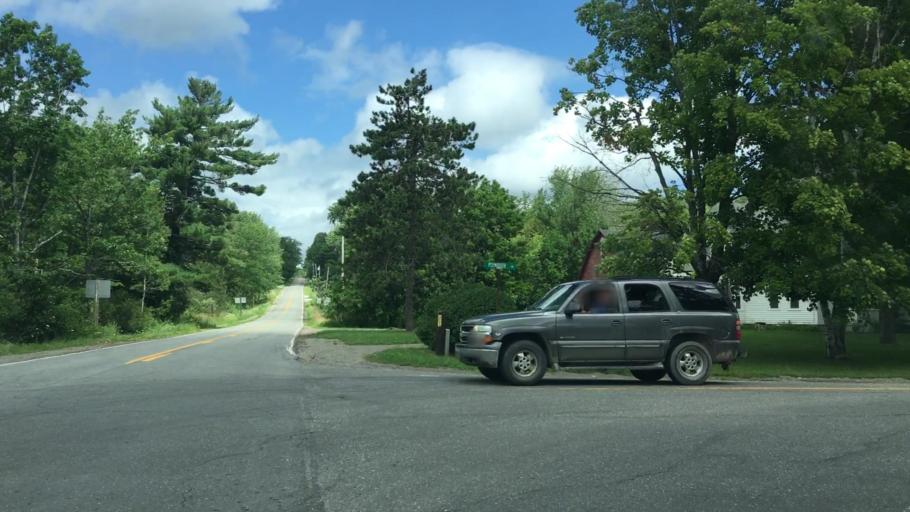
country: US
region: Maine
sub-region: Penobscot County
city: Etna
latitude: 44.7867
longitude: -69.1056
